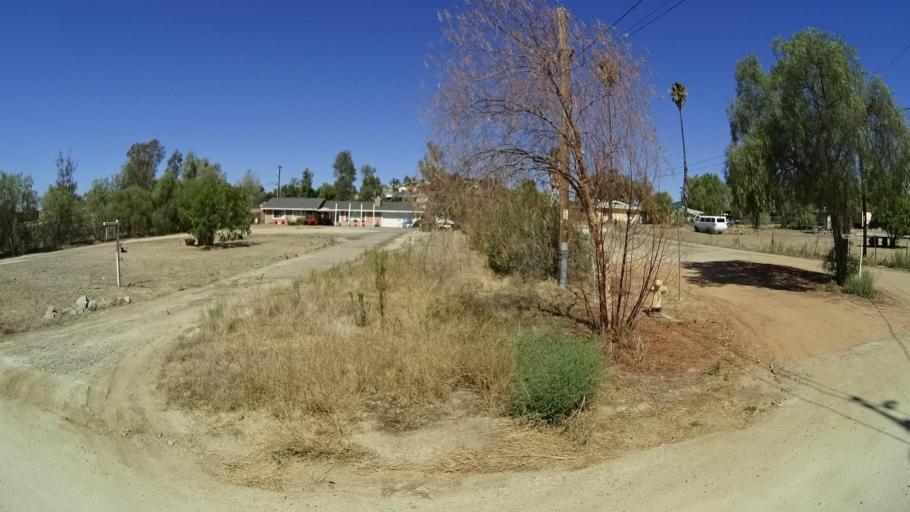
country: US
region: California
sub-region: San Diego County
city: Ramona
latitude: 33.0445
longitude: -116.8526
